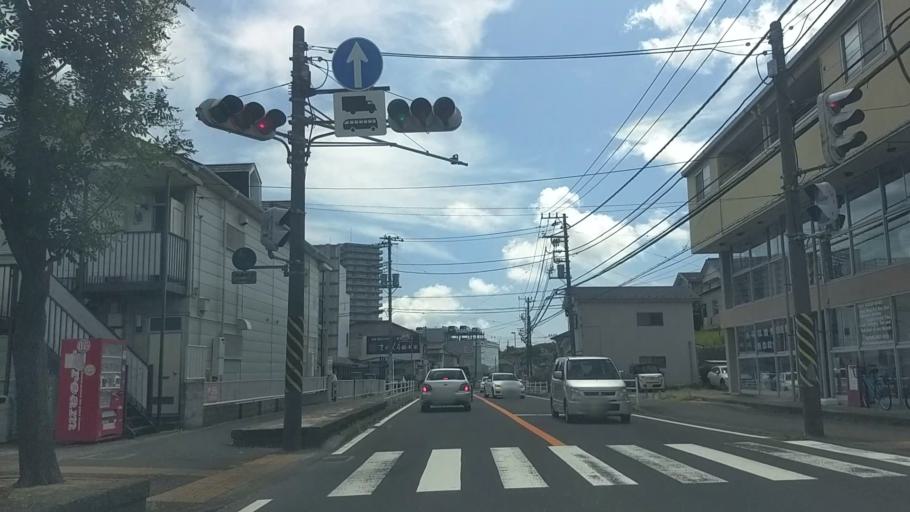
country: JP
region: Kanagawa
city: Yokosuka
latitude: 35.2244
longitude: 139.6448
